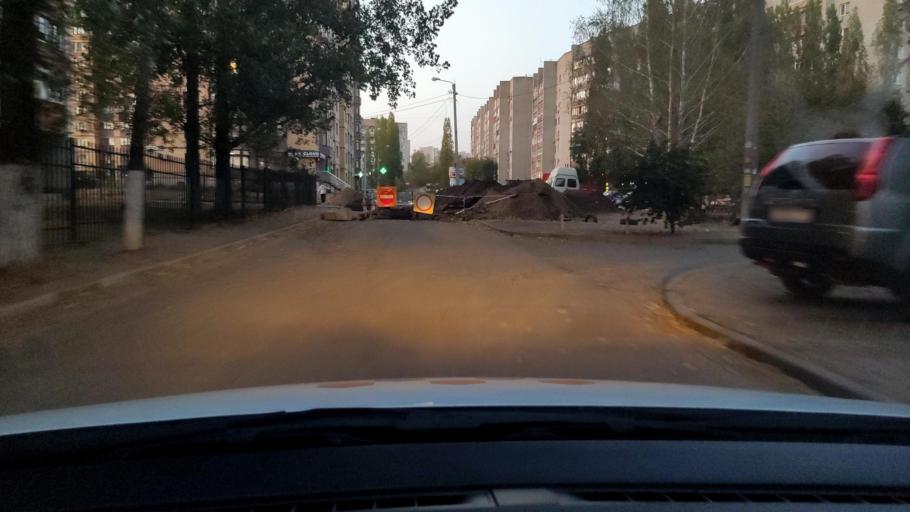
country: RU
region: Voronezj
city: Podgornoye
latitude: 51.6889
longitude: 39.1311
